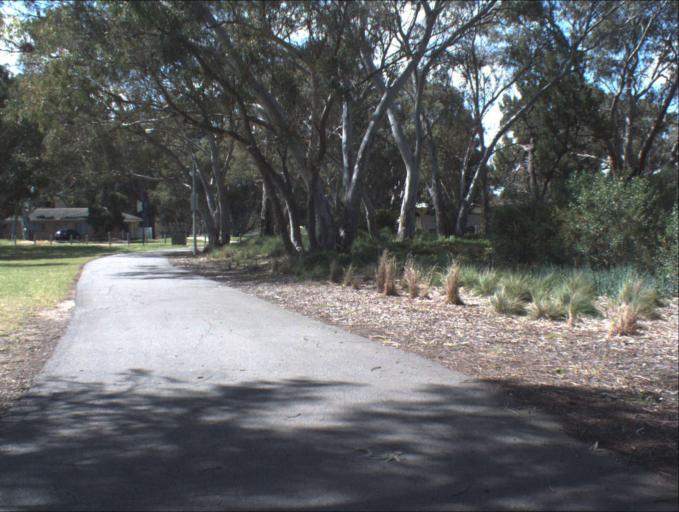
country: AU
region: South Australia
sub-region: Tea Tree Gully
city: Modbury
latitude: -34.8420
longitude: 138.6688
